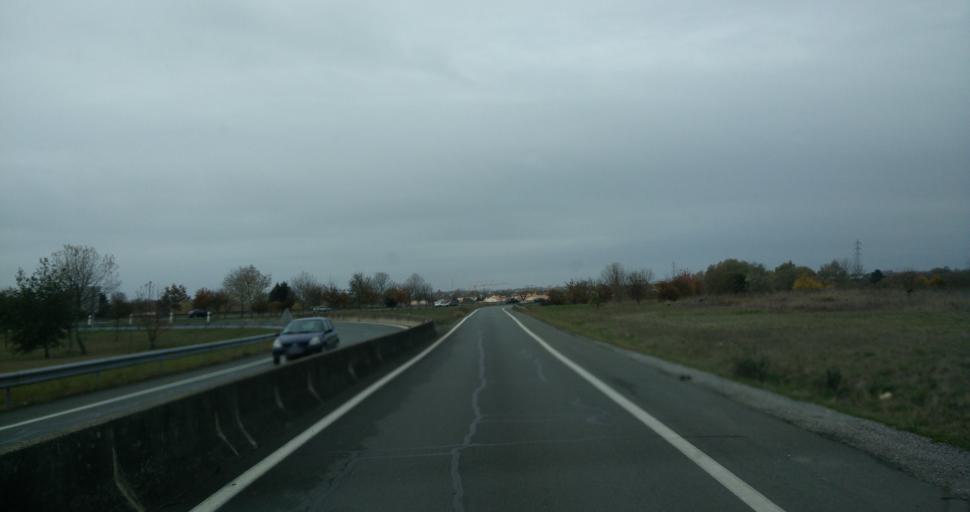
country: FR
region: Poitou-Charentes
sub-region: Departement de la Charente-Maritime
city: Puilboreau
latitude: 46.1777
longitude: -1.1251
